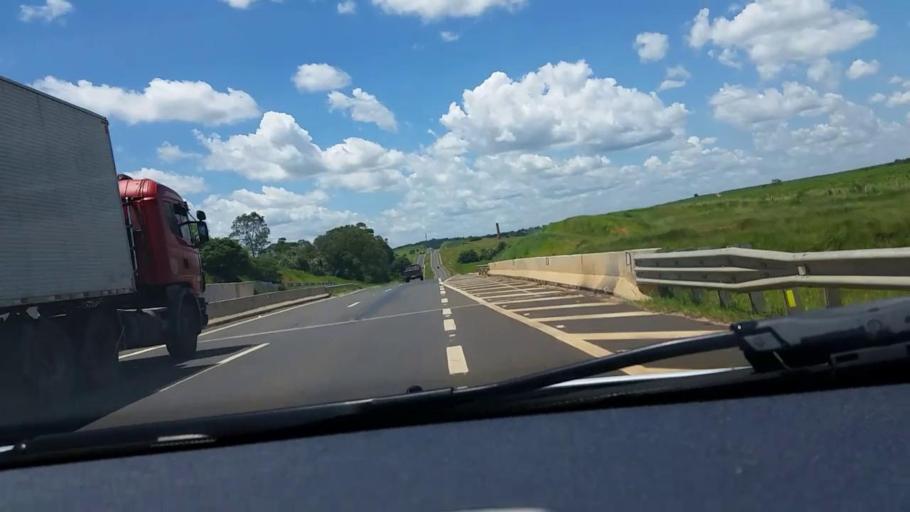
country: BR
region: Sao Paulo
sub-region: Bauru
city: Bauru
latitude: -22.4464
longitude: -49.1597
